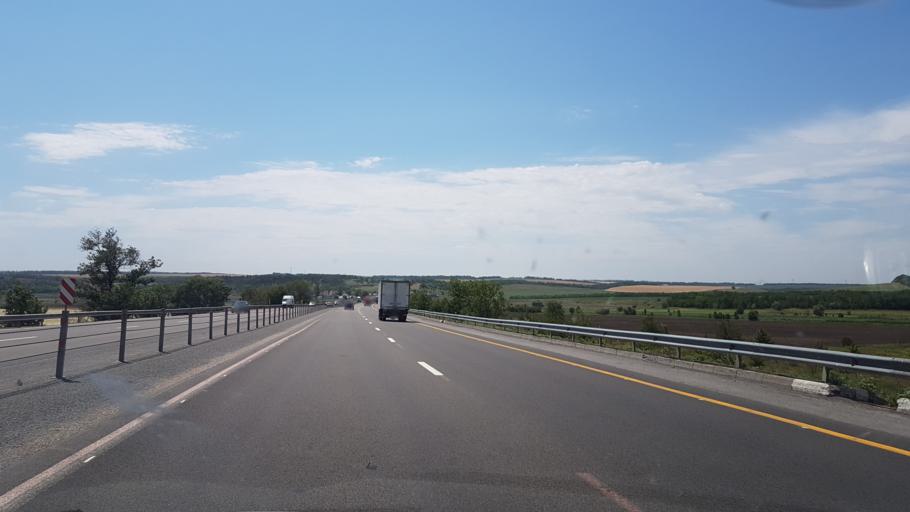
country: RU
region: Rostov
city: Mayskiy
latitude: 47.6547
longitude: 40.0360
